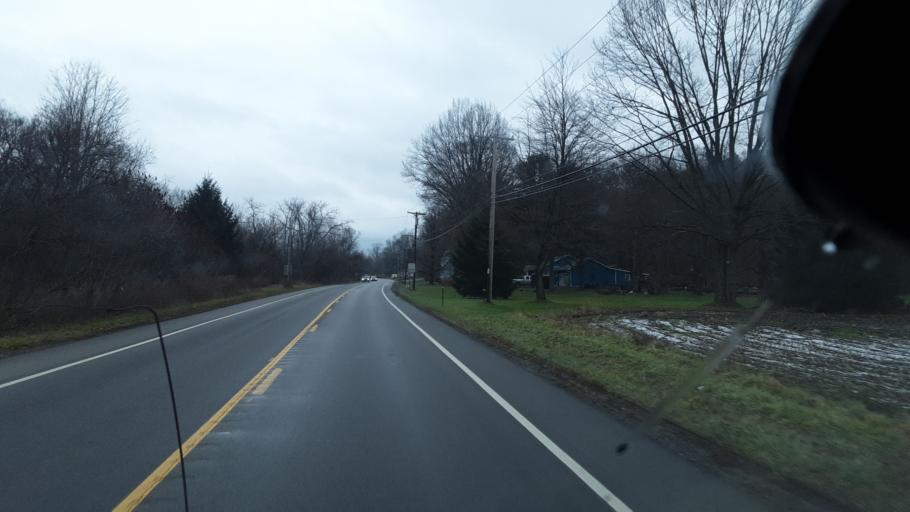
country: US
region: New York
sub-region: Wyoming County
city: Arcade
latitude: 42.4890
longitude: -78.3752
